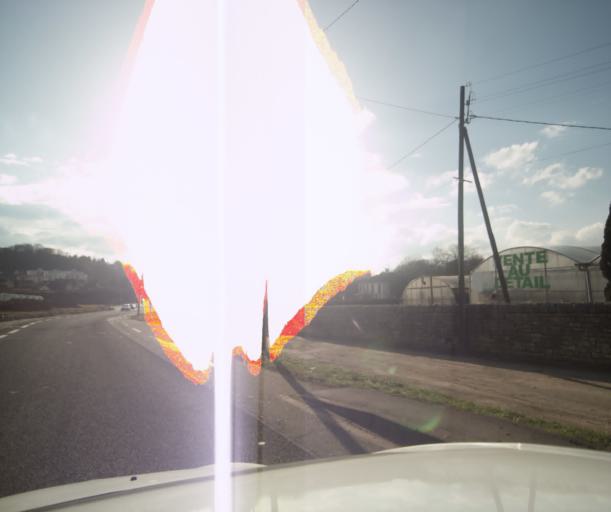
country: FR
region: Franche-Comte
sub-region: Departement du Doubs
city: Besancon
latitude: 47.2521
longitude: 6.0444
